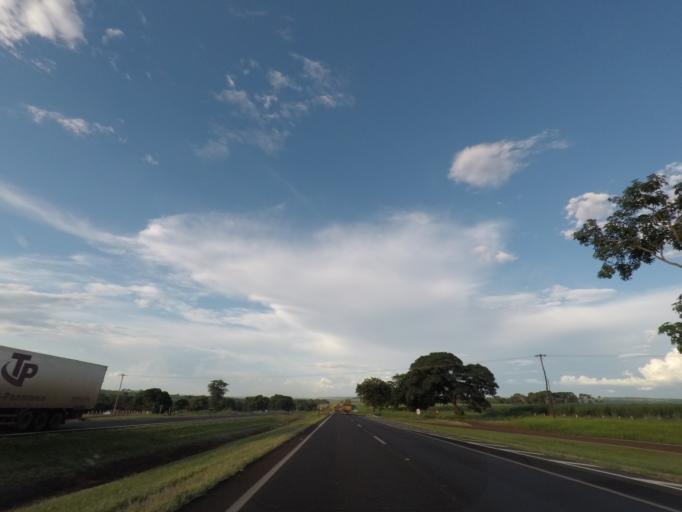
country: BR
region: Sao Paulo
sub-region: Ituverava
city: Ituverava
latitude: -20.3186
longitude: -47.8025
